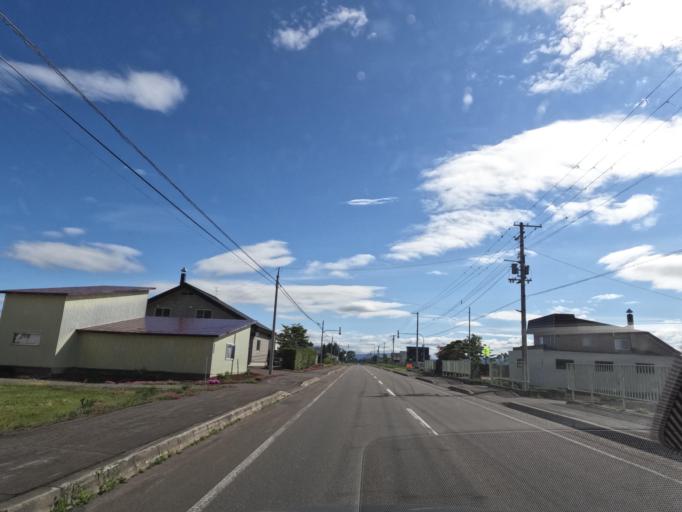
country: JP
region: Hokkaido
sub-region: Asahikawa-shi
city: Asahikawa
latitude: 43.7169
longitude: 142.5281
